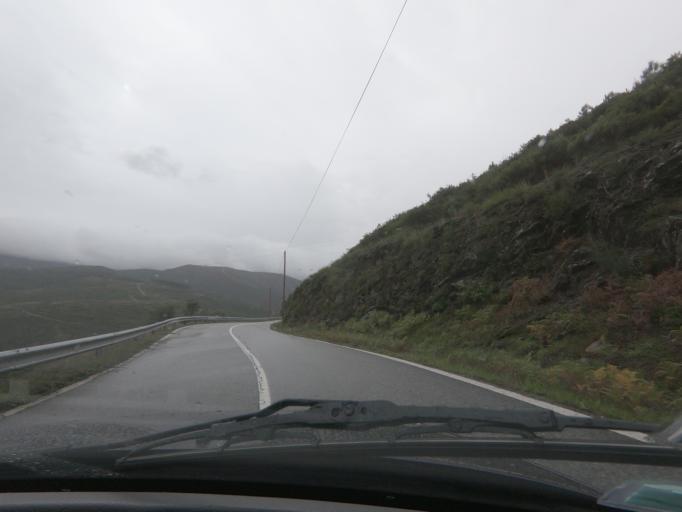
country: PT
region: Vila Real
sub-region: Mondim de Basto
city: Mondim de Basto
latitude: 41.3508
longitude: -7.9025
